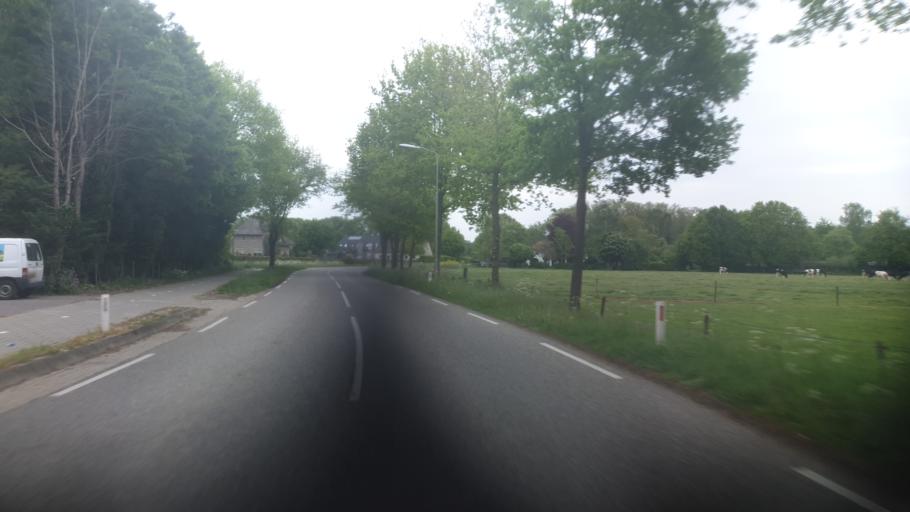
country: NL
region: Gelderland
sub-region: Gemeente Nijmegen
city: Lindenholt
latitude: 51.7770
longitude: 5.7917
